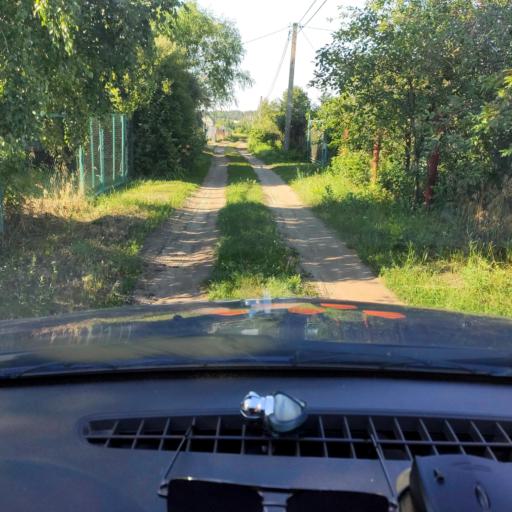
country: RU
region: Voronezj
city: Podgornoye
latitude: 51.8634
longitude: 39.1767
